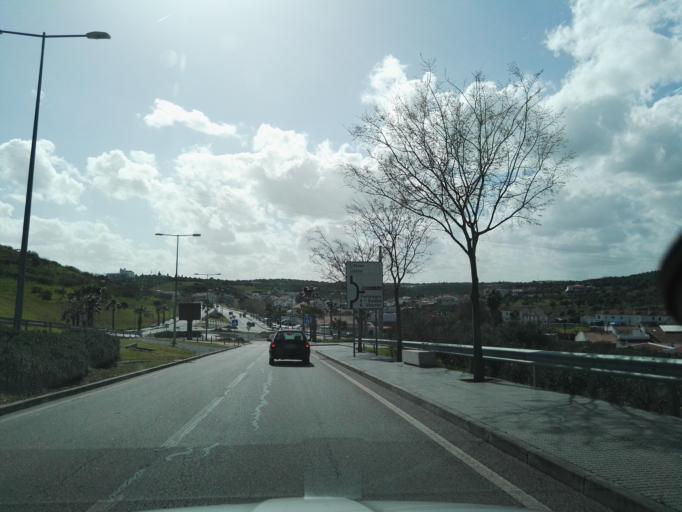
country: PT
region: Portalegre
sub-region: Elvas
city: Elvas
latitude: 38.8855
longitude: -7.1650
